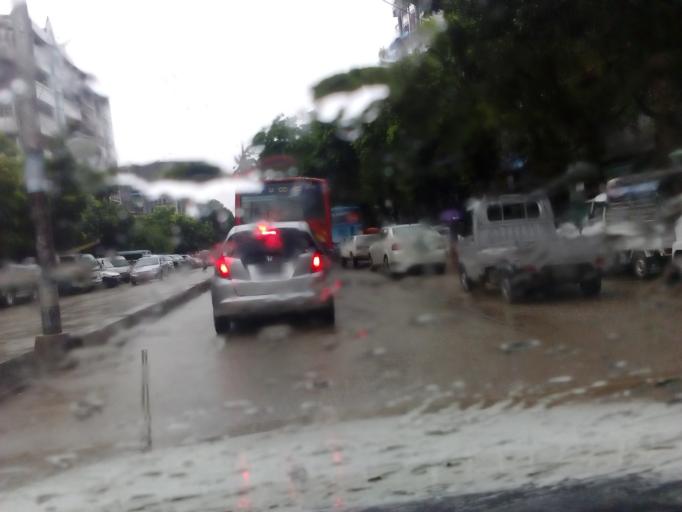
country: MM
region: Yangon
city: Yangon
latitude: 16.8050
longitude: 96.1759
